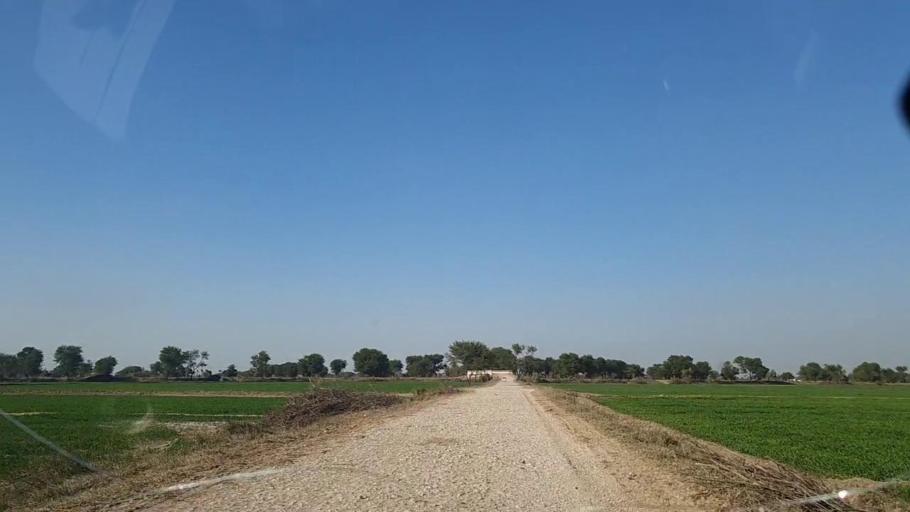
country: PK
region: Sindh
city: Khanpur
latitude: 27.7877
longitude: 69.3519
